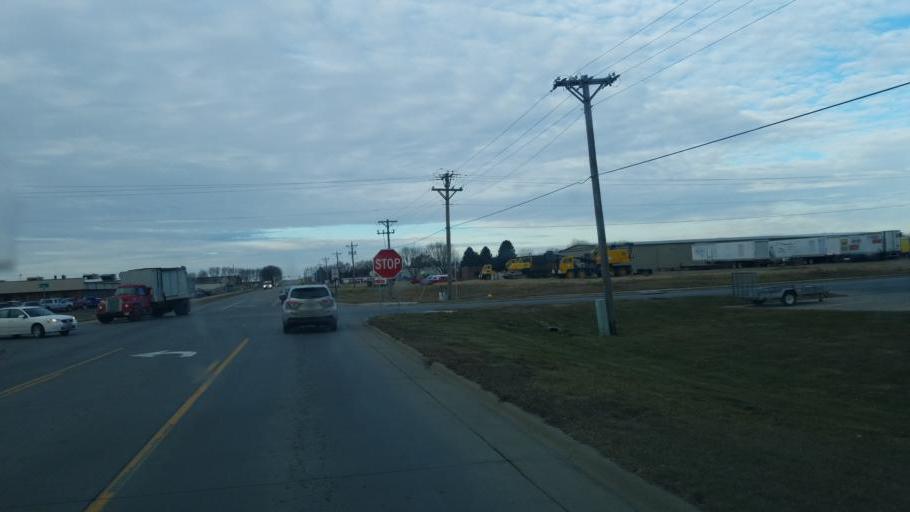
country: US
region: South Dakota
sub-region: Yankton County
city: Yankton
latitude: 42.8944
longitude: -97.4018
